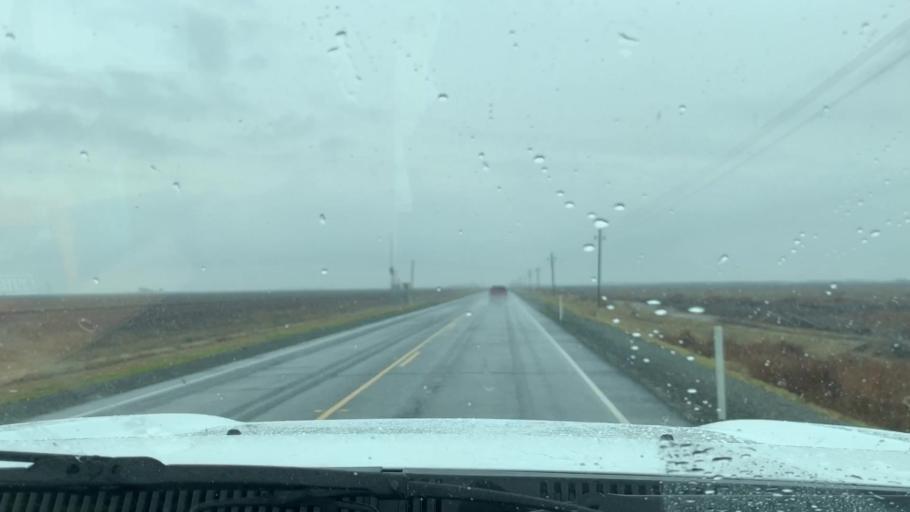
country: US
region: California
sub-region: Tulare County
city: Alpaugh
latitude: 35.9246
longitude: -119.4295
